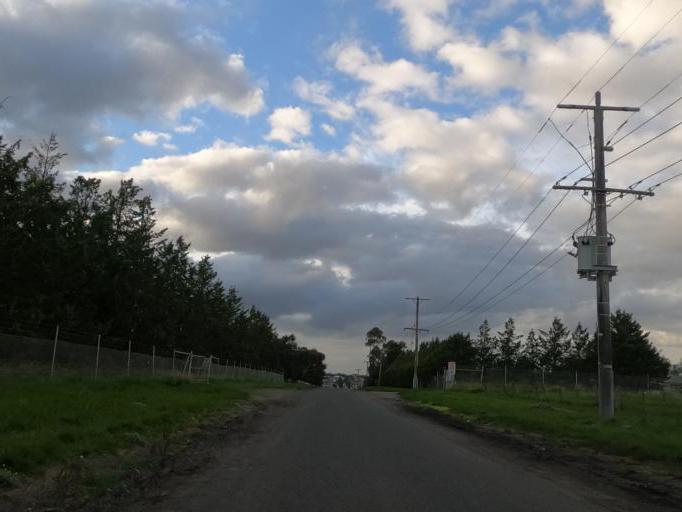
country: AU
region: Victoria
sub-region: Hume
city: Greenvale
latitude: -37.6338
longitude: 144.8853
